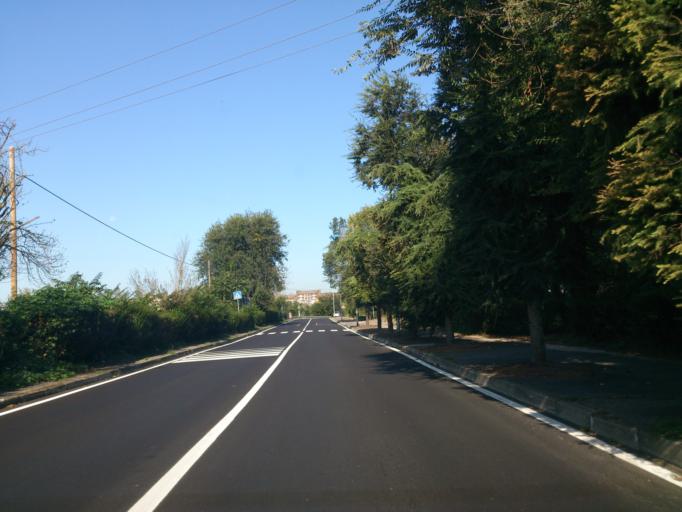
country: IT
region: Lombardy
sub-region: Citta metropolitana di Milano
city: San Giuliano Milanese
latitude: 45.4108
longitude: 9.2846
